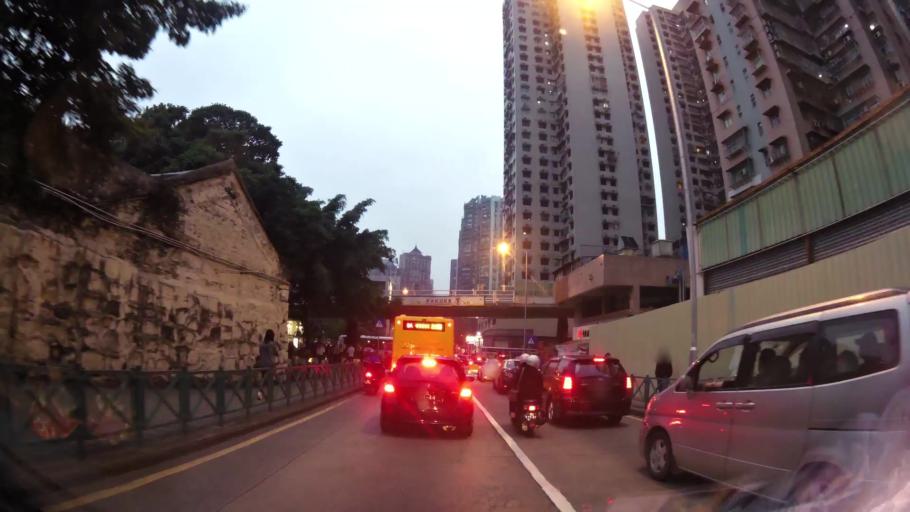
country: MO
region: Macau
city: Macau
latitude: 22.2103
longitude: 113.5479
